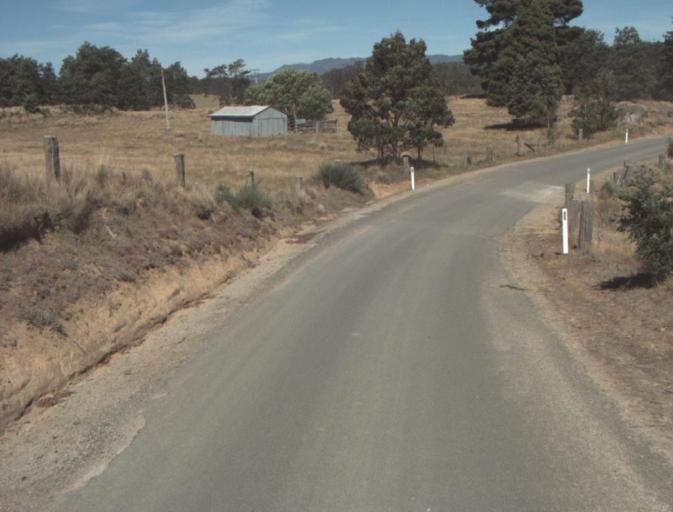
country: AU
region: Tasmania
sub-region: Dorset
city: Scottsdale
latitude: -41.3511
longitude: 147.4506
